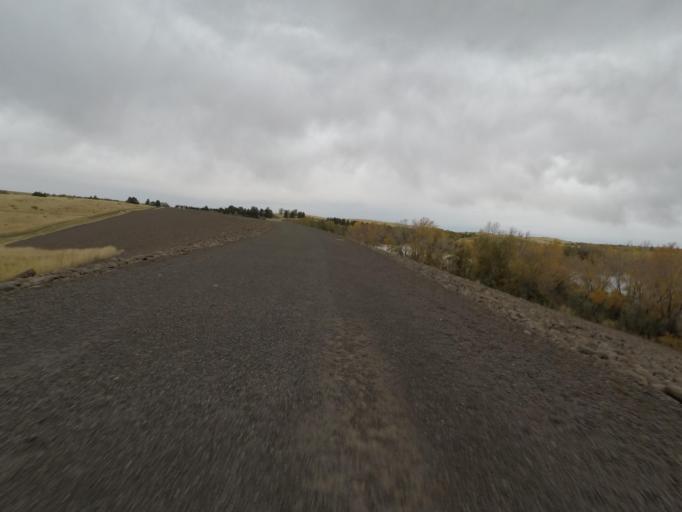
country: US
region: Washington
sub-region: Walla Walla County
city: Walla Walla East
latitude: 46.0622
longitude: -118.2609
